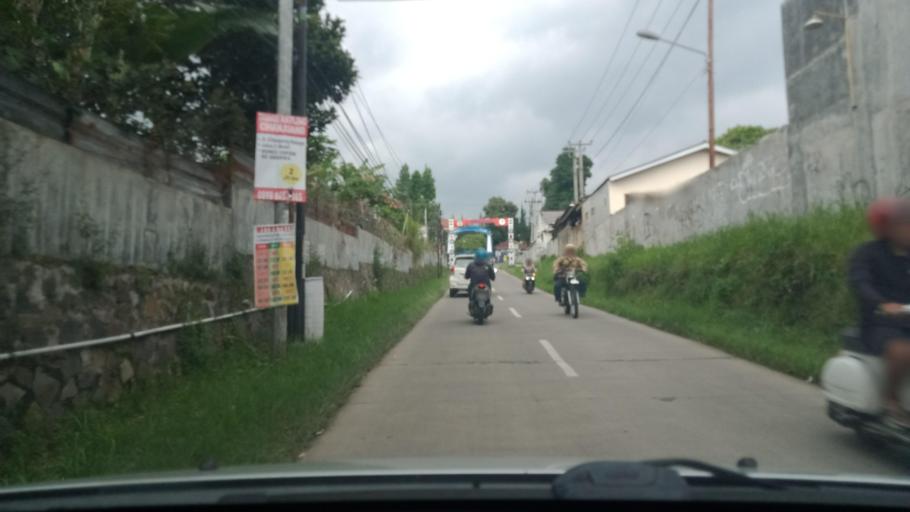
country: ID
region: West Java
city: Lembang
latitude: -6.8034
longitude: 107.5789
